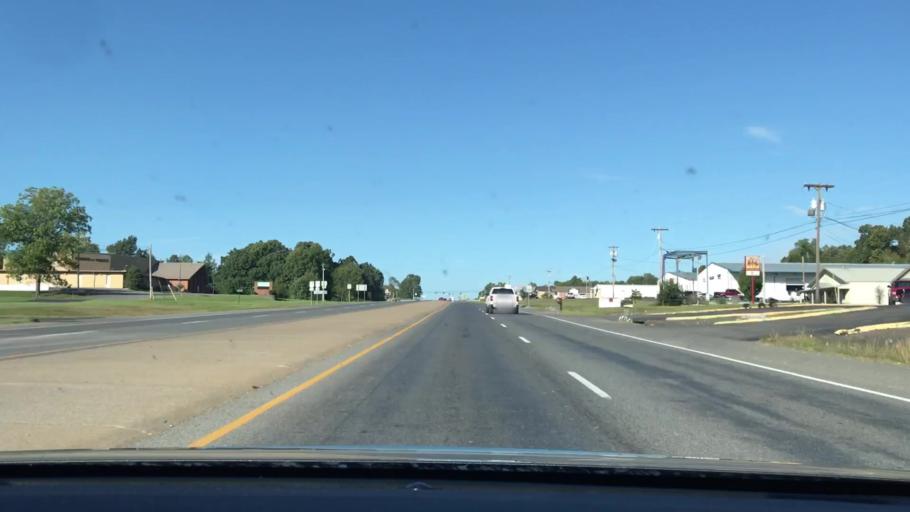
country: US
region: Kentucky
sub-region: Marshall County
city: Calvert City
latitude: 37.0040
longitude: -88.3478
